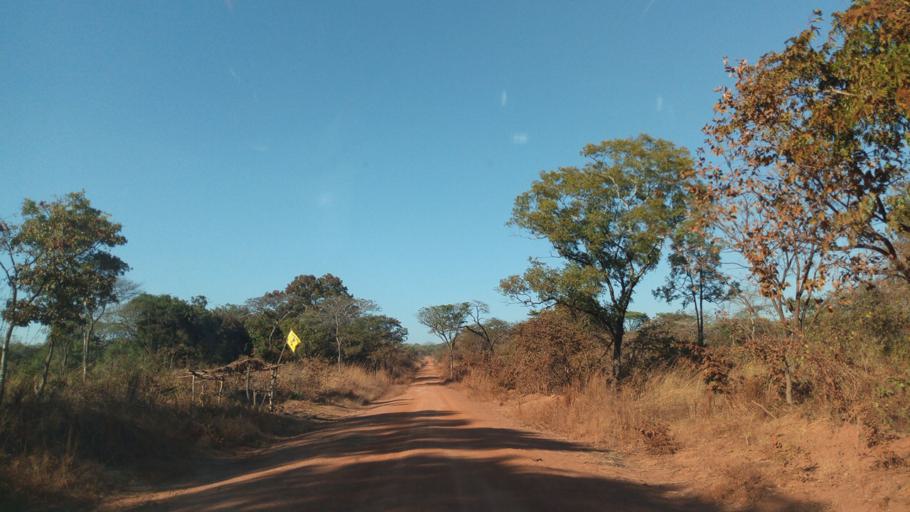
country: ZM
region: Luapula
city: Mwense
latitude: -10.5715
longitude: 28.4348
